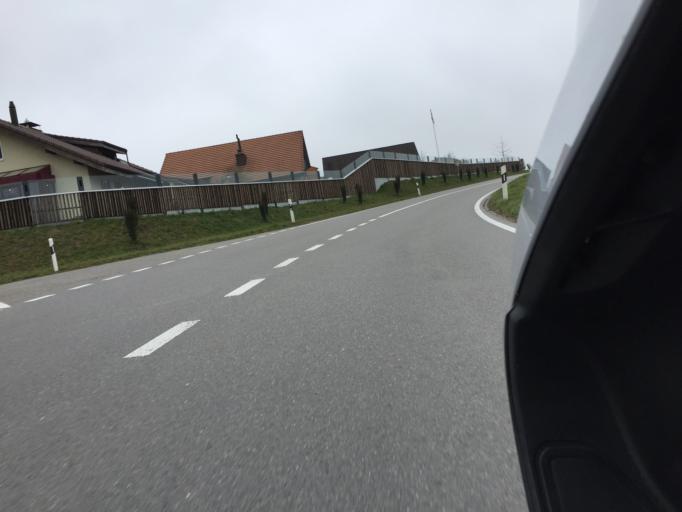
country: CH
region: Bern
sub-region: Biel/Bienne District
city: Meinisberg
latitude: 47.1137
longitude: 7.3521
